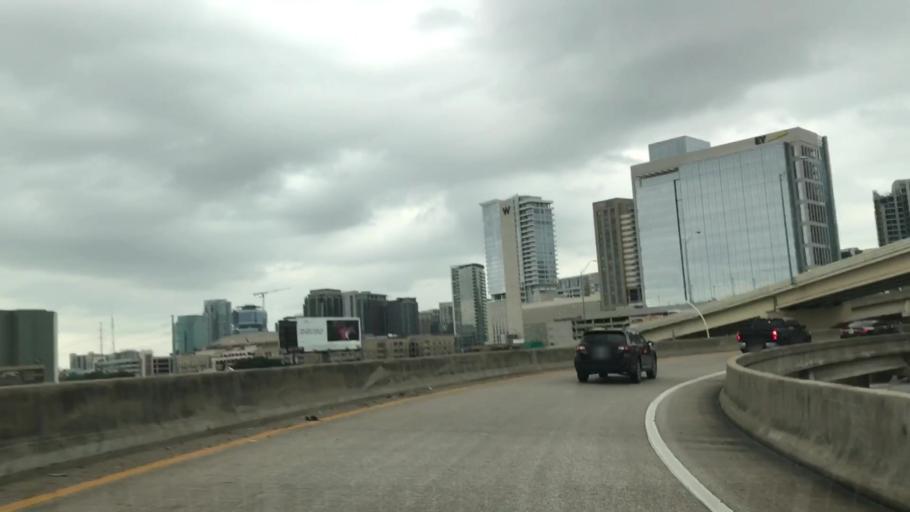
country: US
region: Texas
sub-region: Dallas County
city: Dallas
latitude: 32.7835
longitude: -96.8136
